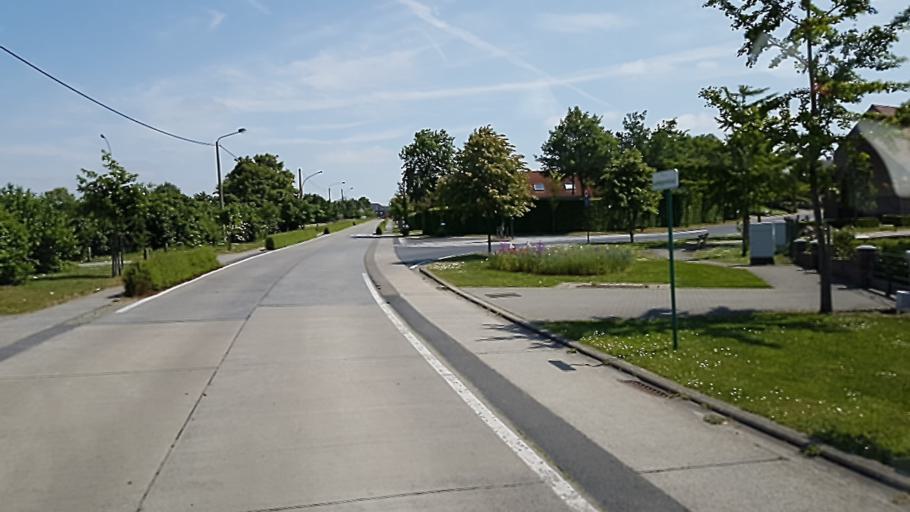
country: BE
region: Flanders
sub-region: Provincie West-Vlaanderen
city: Anzegem
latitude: 50.8372
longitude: 3.4679
